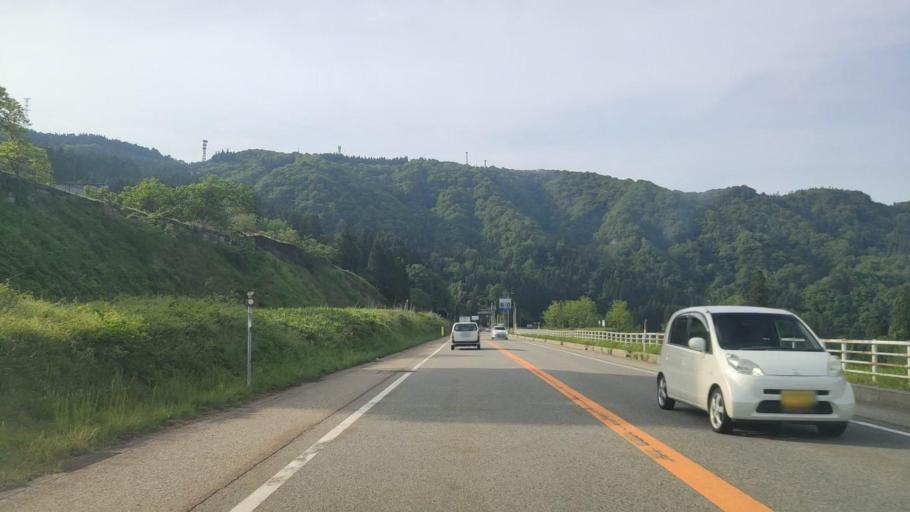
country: JP
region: Toyama
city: Yatsuomachi-higashikumisaka
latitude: 36.4909
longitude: 137.2369
